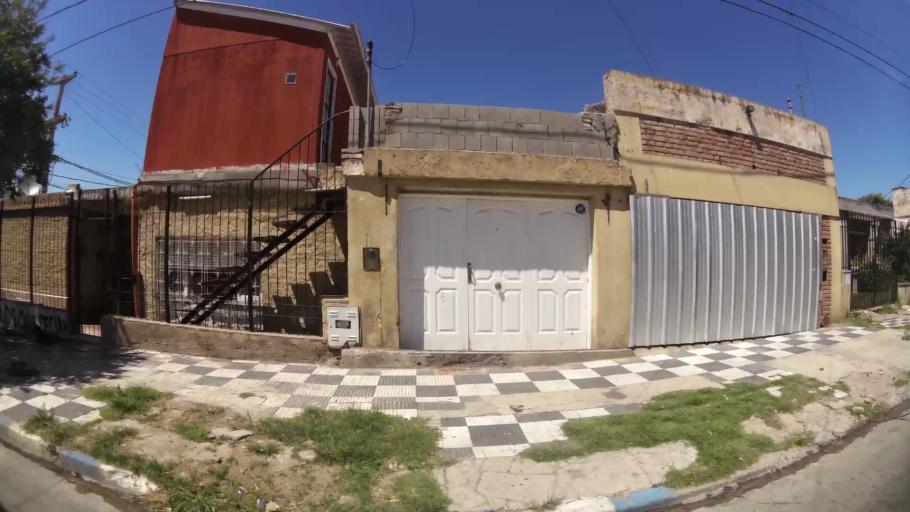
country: AR
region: Cordoba
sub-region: Departamento de Capital
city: Cordoba
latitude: -31.4331
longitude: -64.2077
